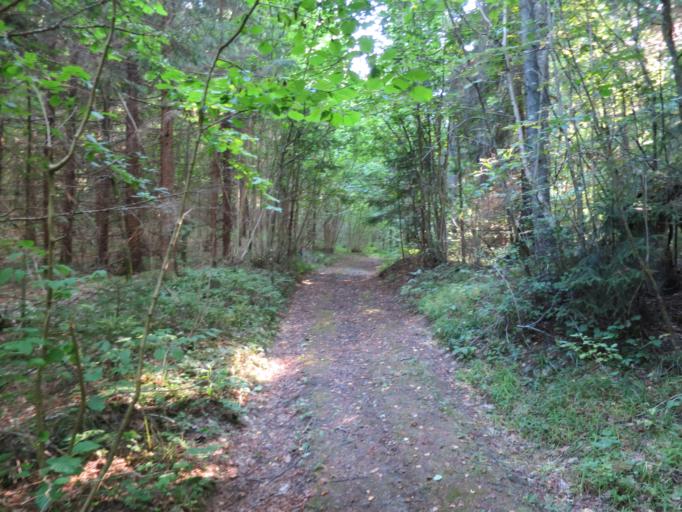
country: LV
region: Ligatne
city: Ligatne
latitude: 57.1266
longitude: 25.1608
